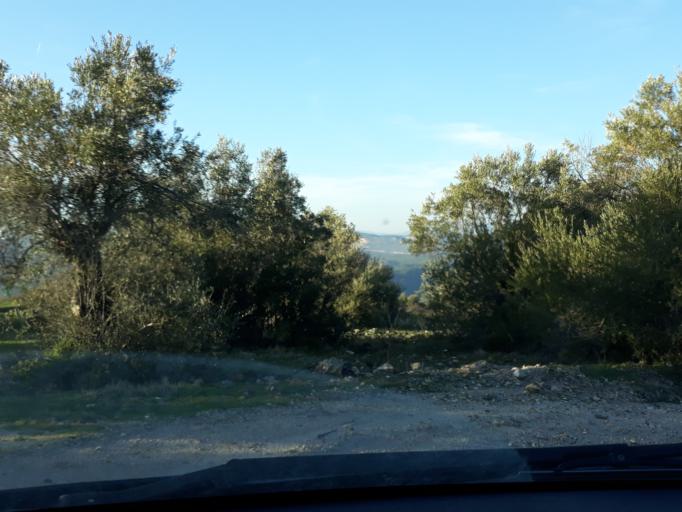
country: GR
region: Central Greece
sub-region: Nomos Voiotias
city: Asopia
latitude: 38.2704
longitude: 23.5286
